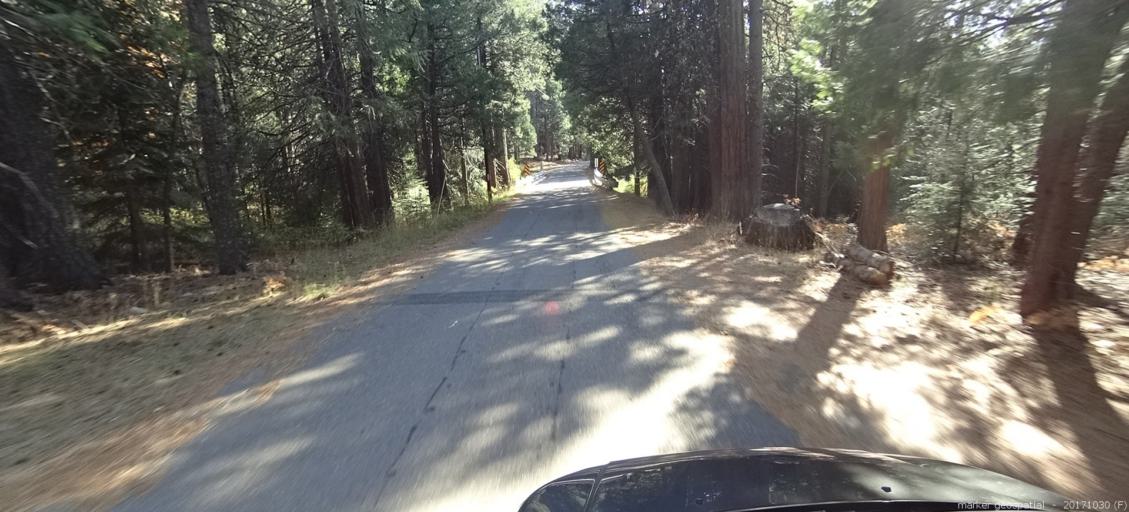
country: US
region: California
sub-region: Shasta County
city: Shingletown
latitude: 40.5109
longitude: -121.7277
